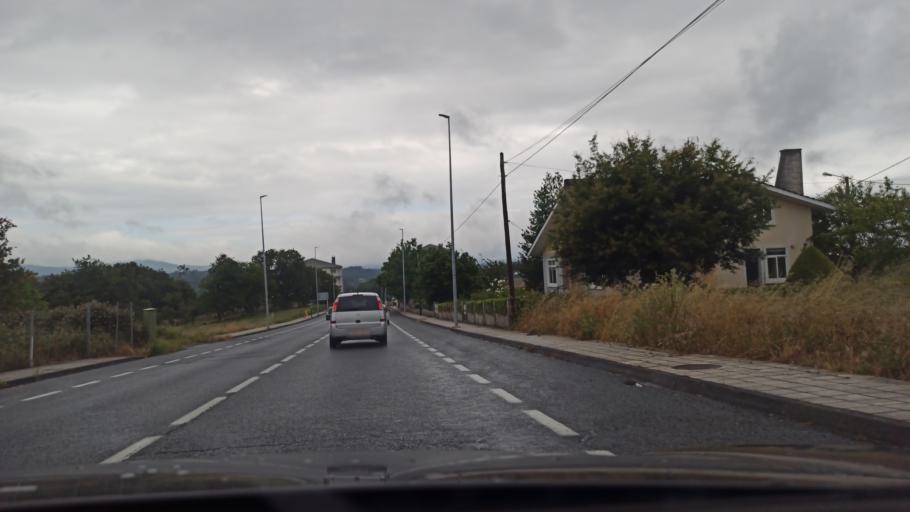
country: ES
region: Galicia
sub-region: Provincia de Lugo
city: Monterroso
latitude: 42.7932
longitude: -7.8405
